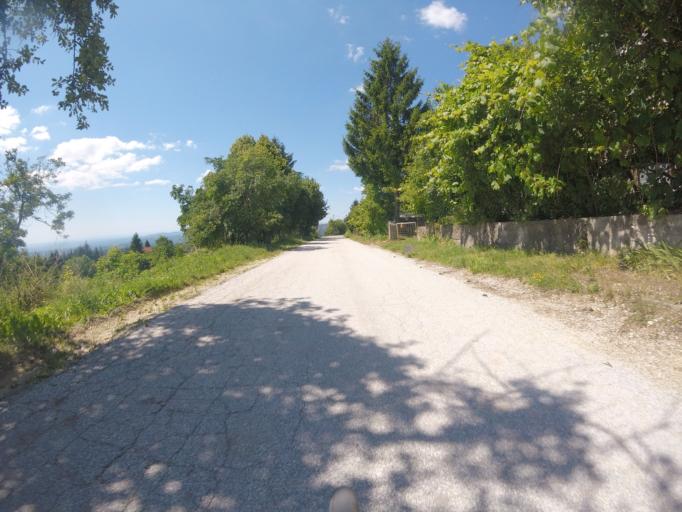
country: SI
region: Kostanjevica na Krki
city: Kostanjevica na Krki
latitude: 45.7700
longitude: 15.4635
